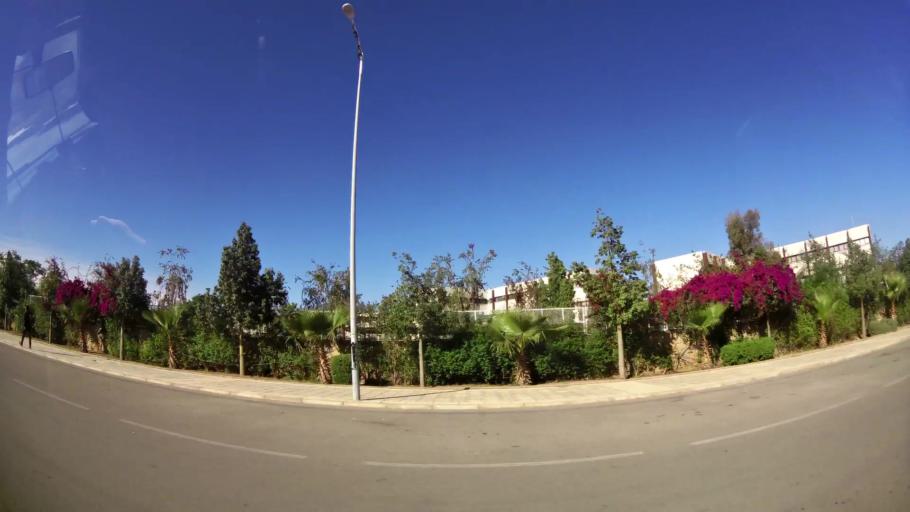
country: MA
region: Oriental
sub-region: Oujda-Angad
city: Oujda
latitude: 34.6535
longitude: -1.8976
